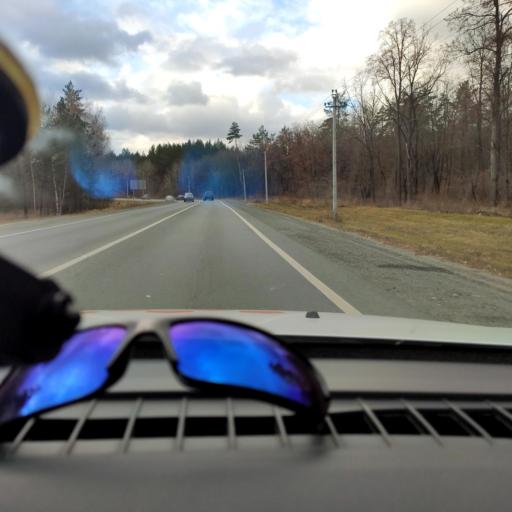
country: RU
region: Samara
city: Volzhskiy
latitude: 53.4487
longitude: 50.1235
